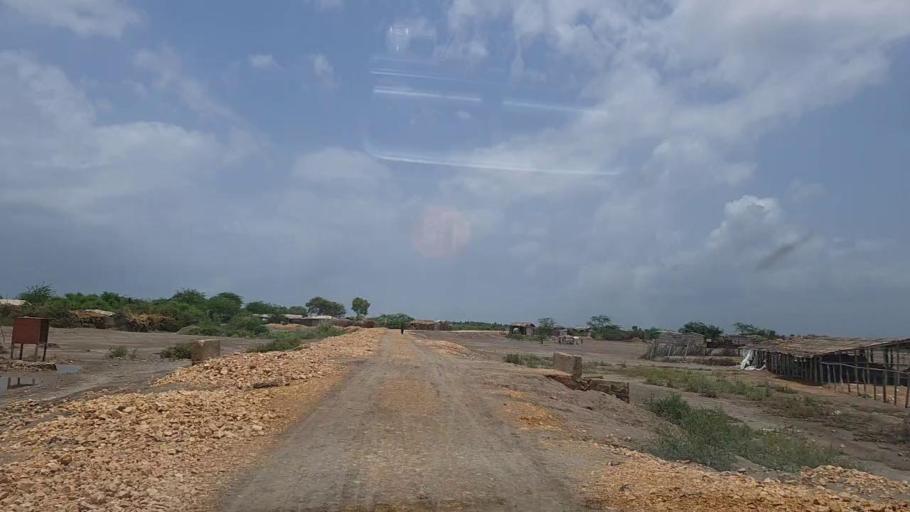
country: PK
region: Sindh
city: Thatta
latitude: 24.6206
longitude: 68.0333
